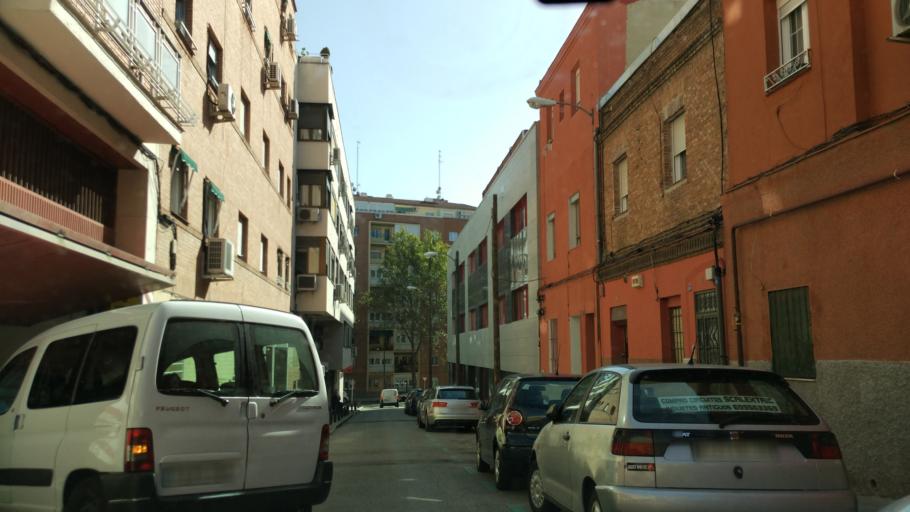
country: ES
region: Madrid
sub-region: Provincia de Madrid
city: Tetuan de las Victorias
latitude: 40.4589
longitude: -3.6982
